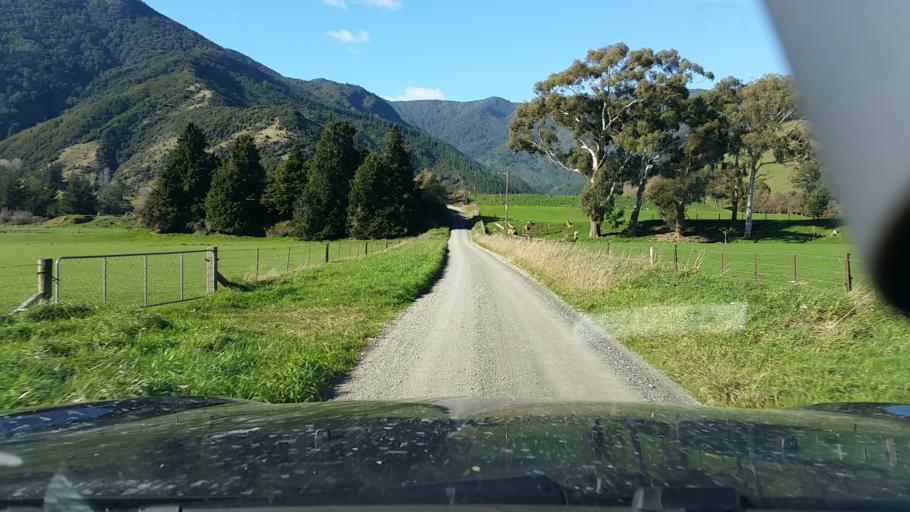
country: NZ
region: Marlborough
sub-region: Marlborough District
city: Picton
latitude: -41.3322
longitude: 173.7671
